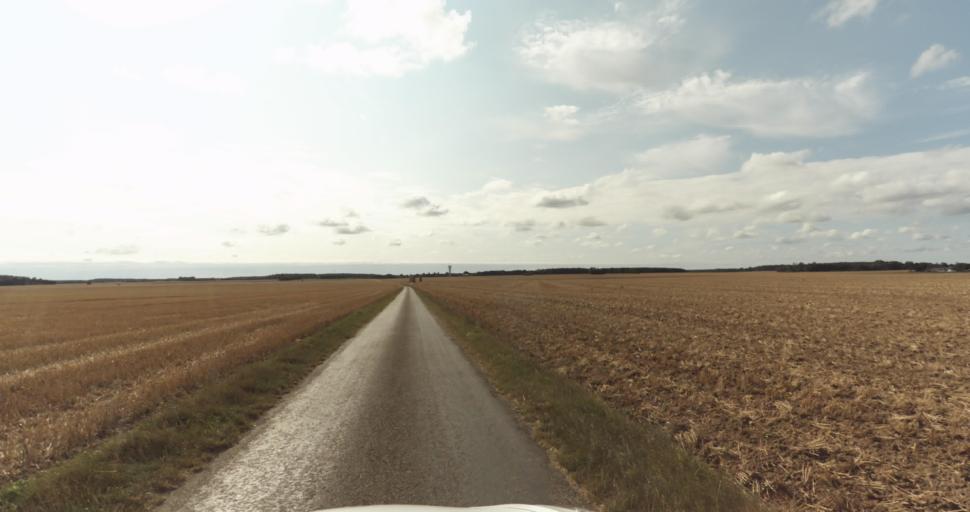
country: FR
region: Haute-Normandie
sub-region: Departement de l'Eure
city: Tillieres-sur-Avre
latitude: 48.7865
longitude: 1.0644
